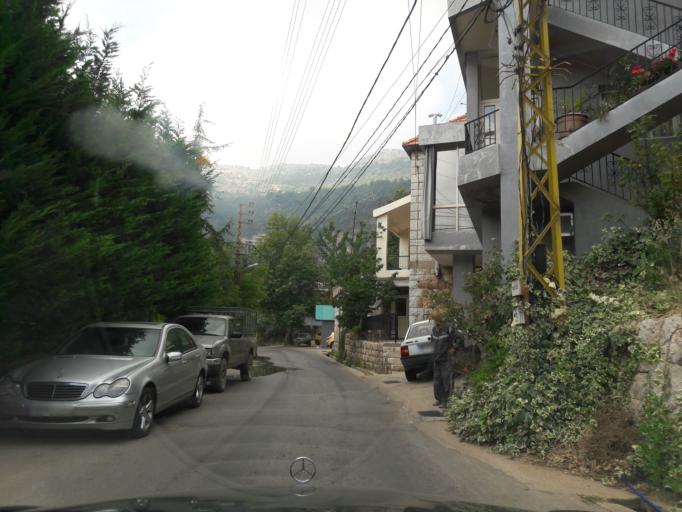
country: LB
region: Beqaa
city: Zahle
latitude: 33.9425
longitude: 35.8000
